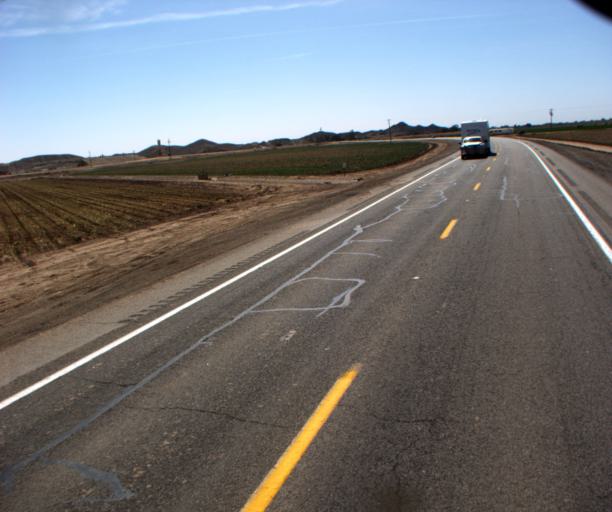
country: US
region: Arizona
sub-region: Yuma County
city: Fortuna Foothills
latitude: 32.7567
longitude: -114.4179
